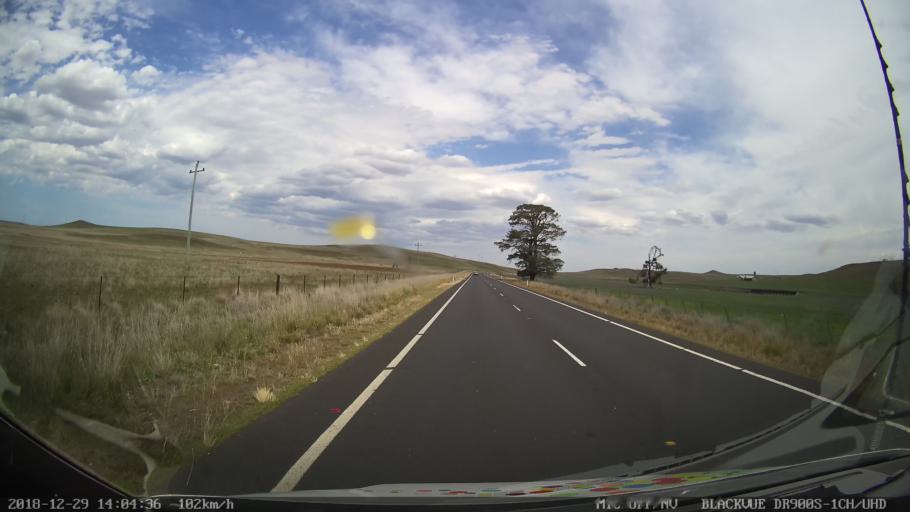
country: AU
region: New South Wales
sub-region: Cooma-Monaro
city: Cooma
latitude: -36.3184
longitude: 149.1875
